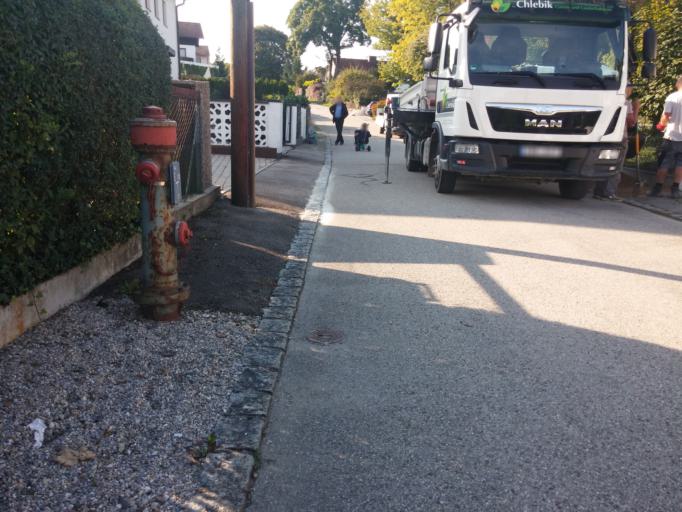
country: DE
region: Bavaria
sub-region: Upper Bavaria
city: Kirchseeon
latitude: 48.0817
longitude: 11.8724
